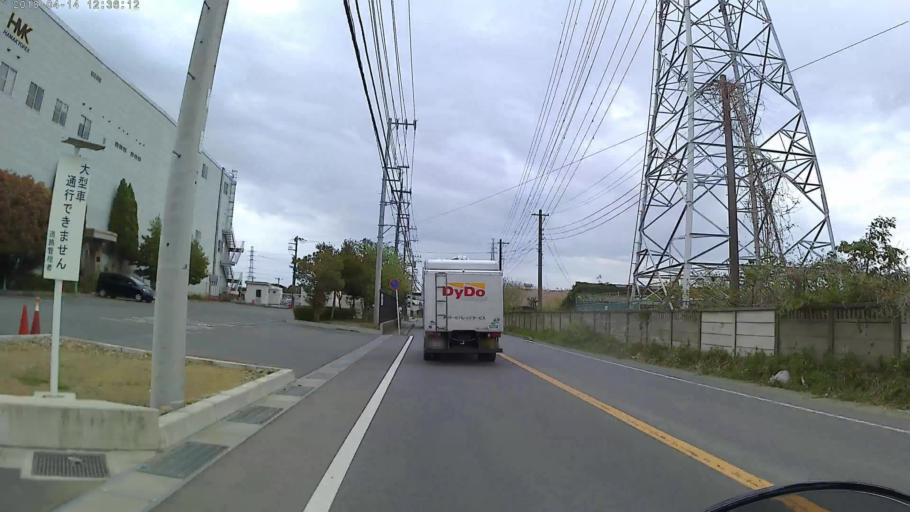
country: JP
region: Kanagawa
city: Atsugi
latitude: 35.4171
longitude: 139.4079
